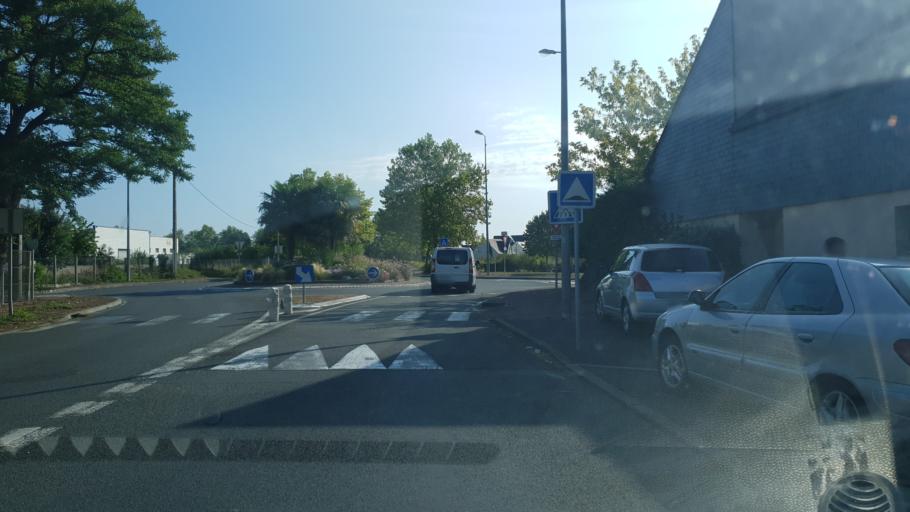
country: FR
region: Centre
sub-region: Departement d'Indre-et-Loire
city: La Ville-aux-Dames
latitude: 47.3887
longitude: 0.7664
